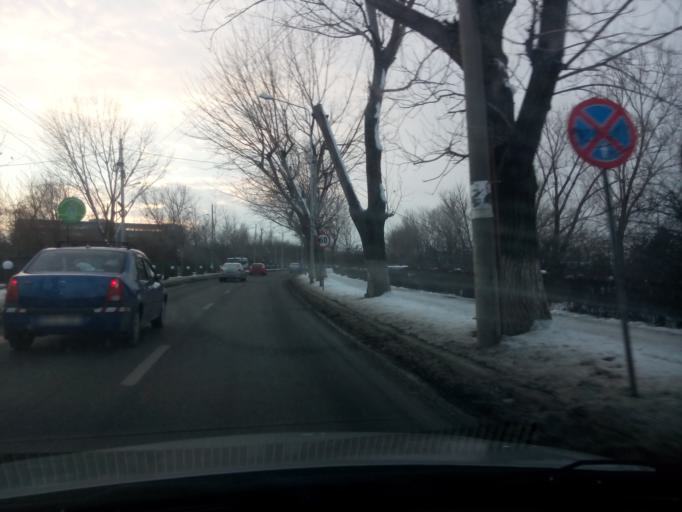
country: RO
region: Ilfov
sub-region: Comuna Pantelimon
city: Pantelimon
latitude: 44.4422
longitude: 26.1971
